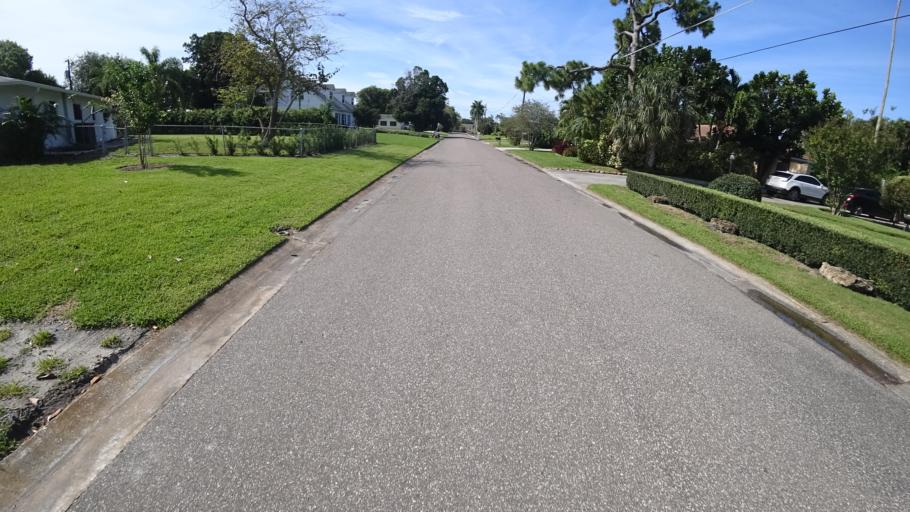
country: US
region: Florida
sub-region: Manatee County
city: West Bradenton
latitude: 27.5170
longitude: -82.6397
